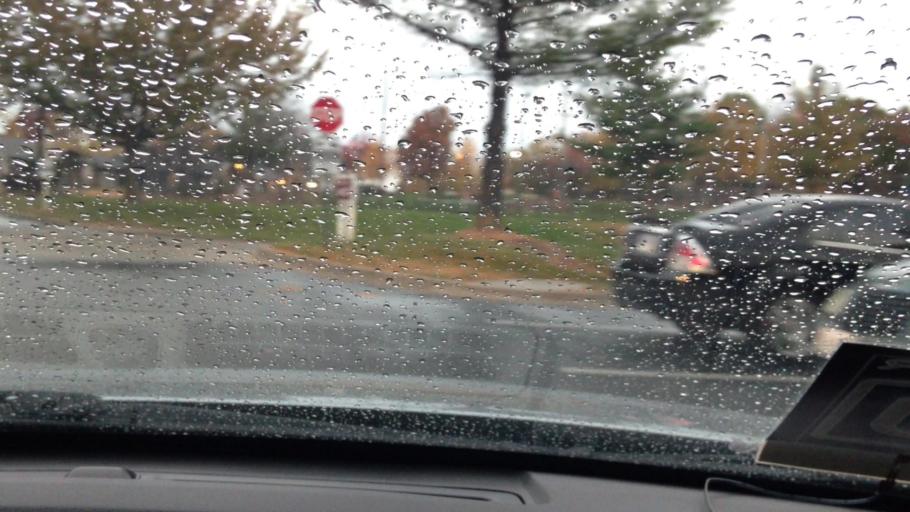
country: US
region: Missouri
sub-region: Platte County
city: Riverside
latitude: 39.2100
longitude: -94.6324
